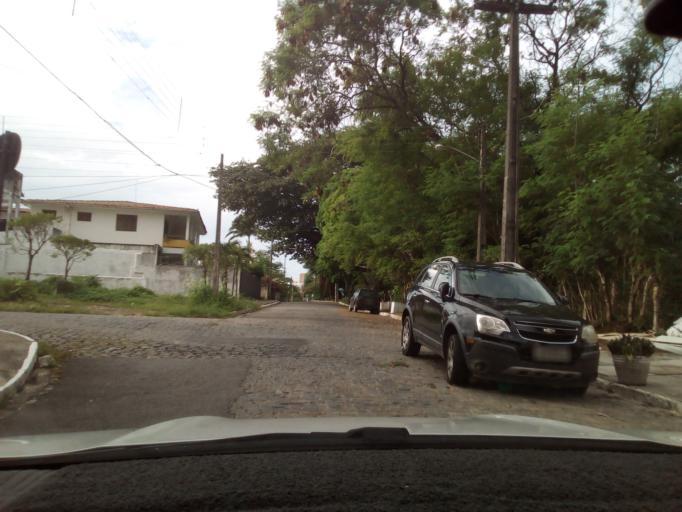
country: BR
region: Paraiba
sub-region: Joao Pessoa
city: Joao Pessoa
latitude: -7.1145
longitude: -34.8362
